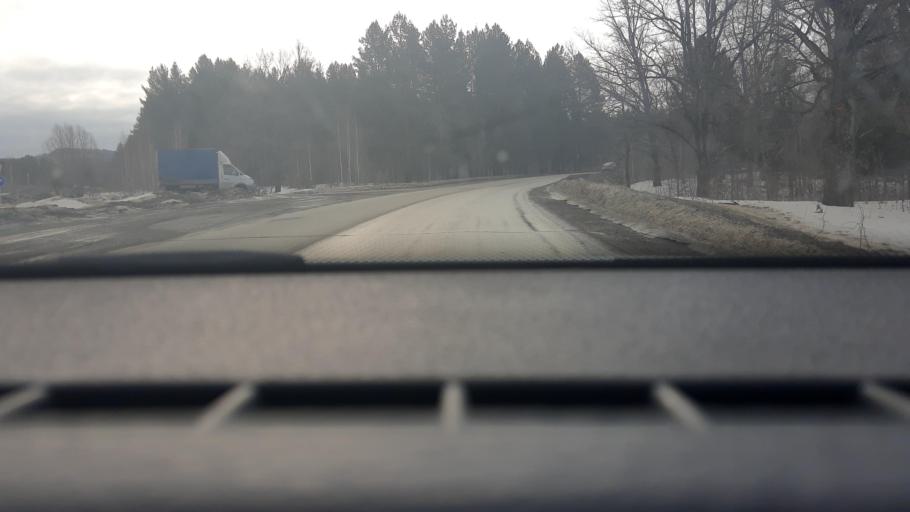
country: RU
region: Chelyabinsk
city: Asha
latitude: 54.9712
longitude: 57.2875
